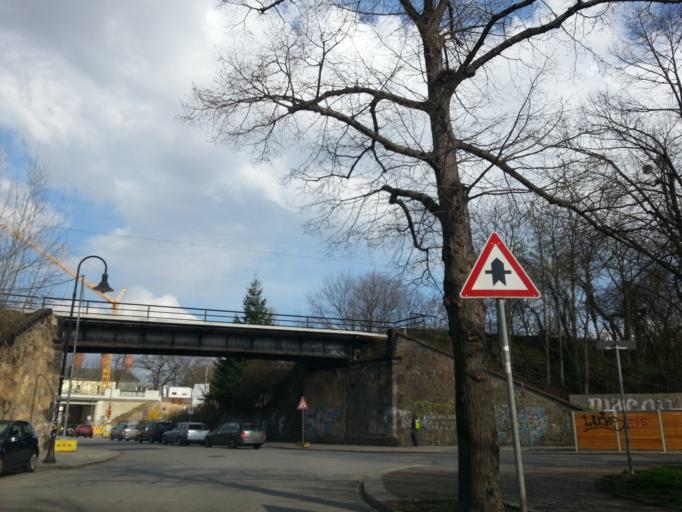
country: DE
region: Saxony
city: Dresden
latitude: 51.0808
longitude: 13.7248
